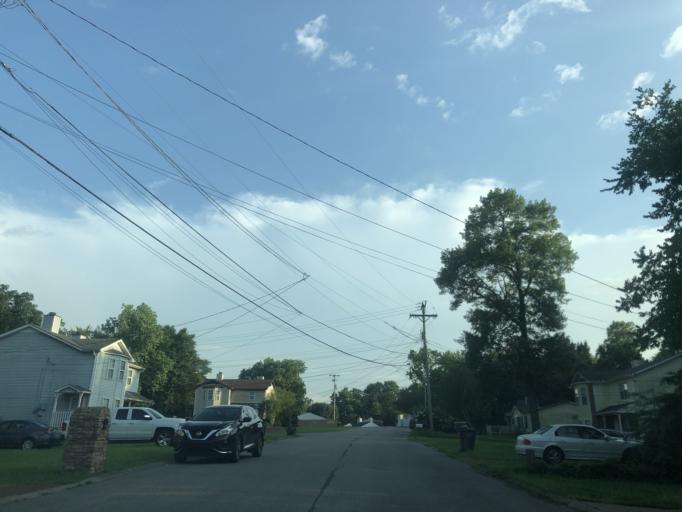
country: US
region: Tennessee
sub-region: Davidson County
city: Lakewood
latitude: 36.1462
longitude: -86.6407
